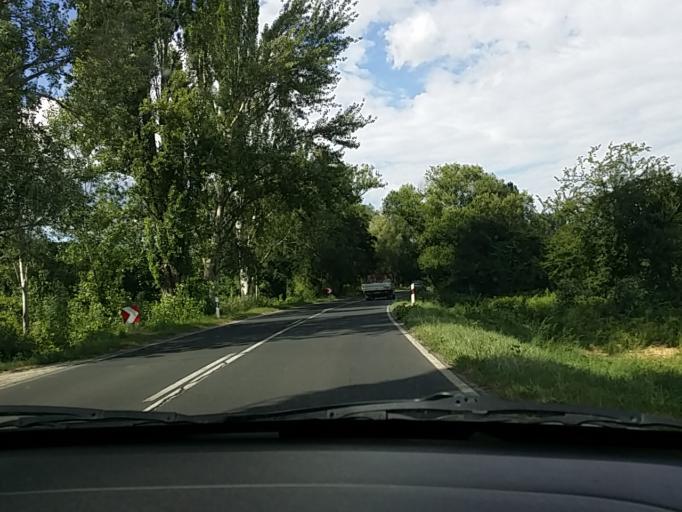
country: HU
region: Veszprem
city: Revfueloep
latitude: 46.8442
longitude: 17.6528
